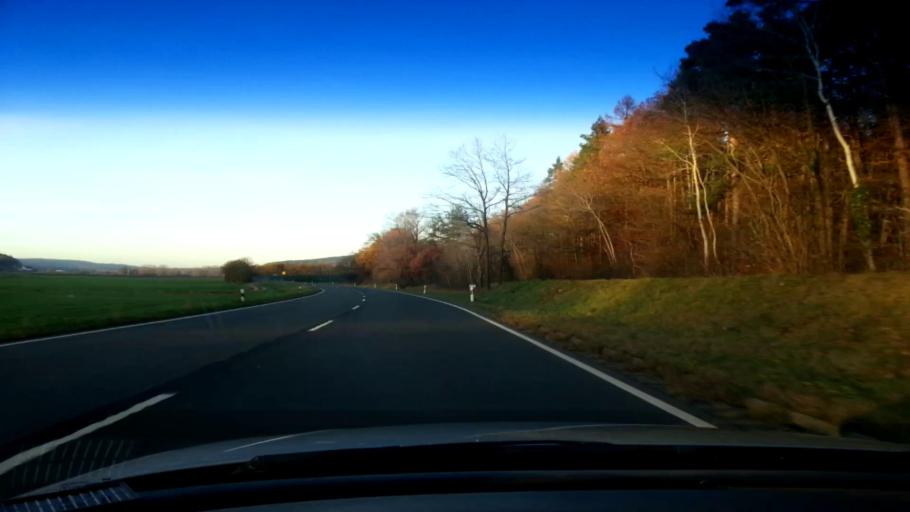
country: DE
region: Bavaria
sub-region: Upper Franconia
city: Rattelsdorf
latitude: 50.0380
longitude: 10.8825
